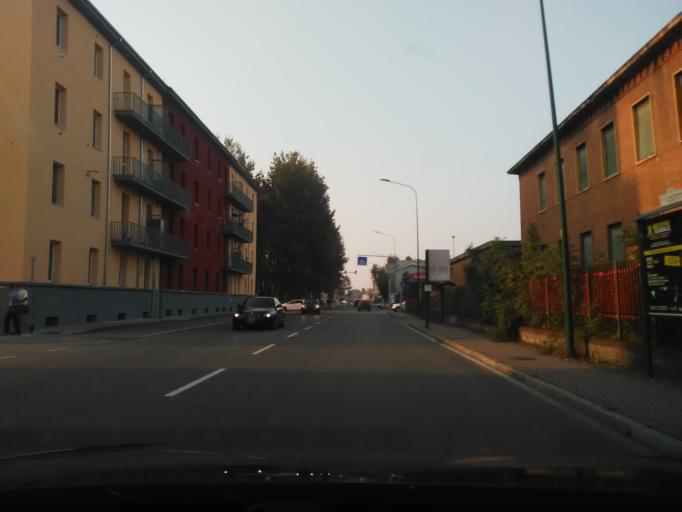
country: IT
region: Piedmont
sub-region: Provincia di Alessandria
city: Casale Monferrato
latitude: 45.1448
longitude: 8.4461
